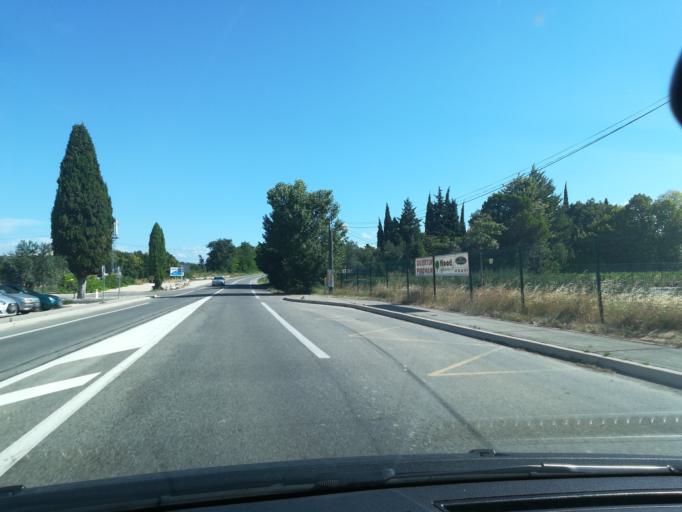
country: FR
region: Provence-Alpes-Cote d'Azur
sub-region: Departement du Vaucluse
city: Sablet
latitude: 44.2216
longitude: 5.0079
